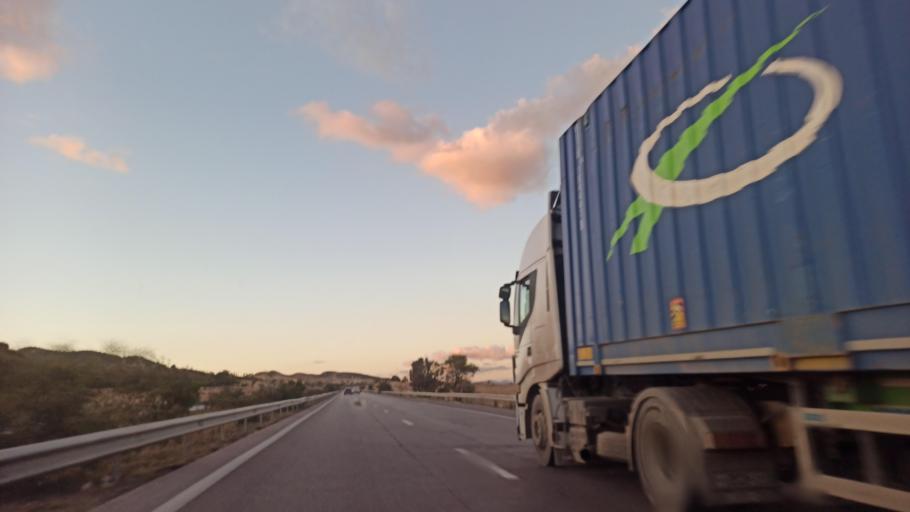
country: TN
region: Susah
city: Harqalah
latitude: 36.2231
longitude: 10.4167
